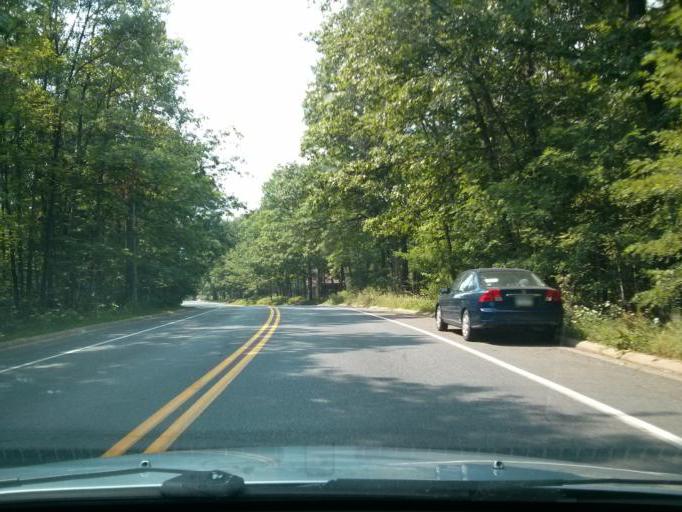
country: US
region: Pennsylvania
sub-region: Centre County
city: Park Forest Village
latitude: 40.8236
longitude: -77.8870
